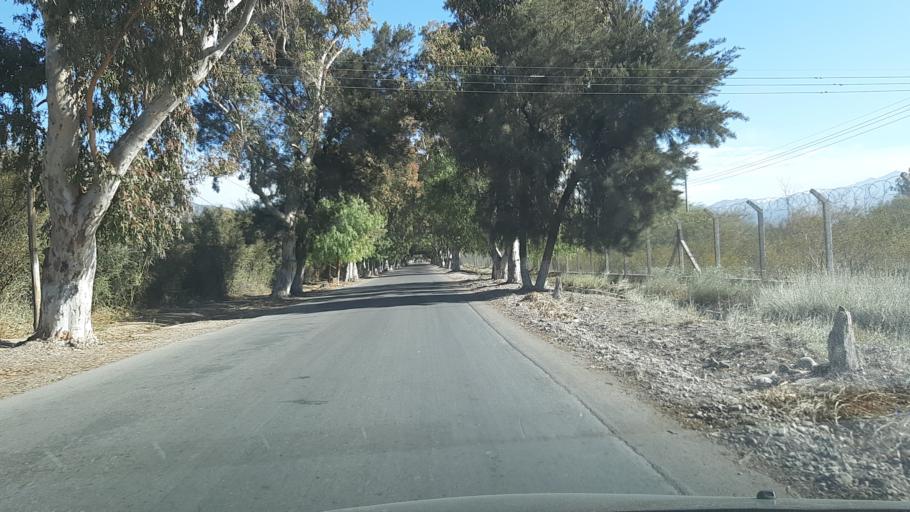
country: AR
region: San Juan
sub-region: Departamento de Zonda
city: Zonda
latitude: -31.5464
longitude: -68.7226
